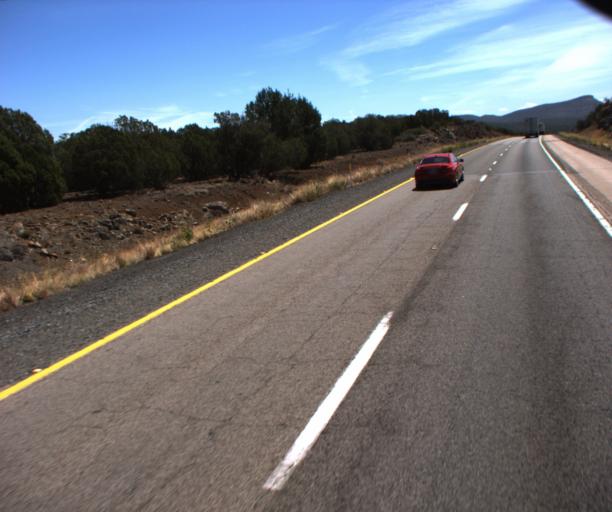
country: US
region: Arizona
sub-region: Mohave County
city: Peach Springs
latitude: 35.1904
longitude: -113.3304
